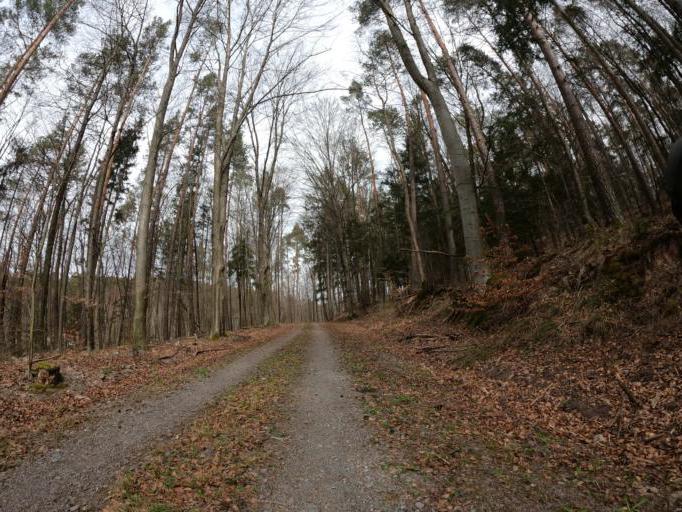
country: DE
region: Baden-Wuerttemberg
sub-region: Regierungsbezirk Stuttgart
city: Waldenbuch
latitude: 48.6356
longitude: 9.1723
